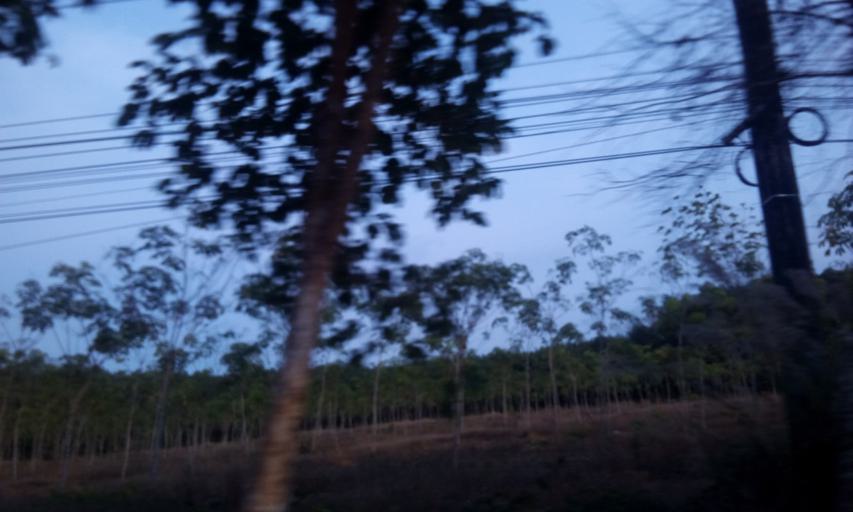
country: TH
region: Trat
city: Khao Saming
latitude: 12.3362
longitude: 102.3706
